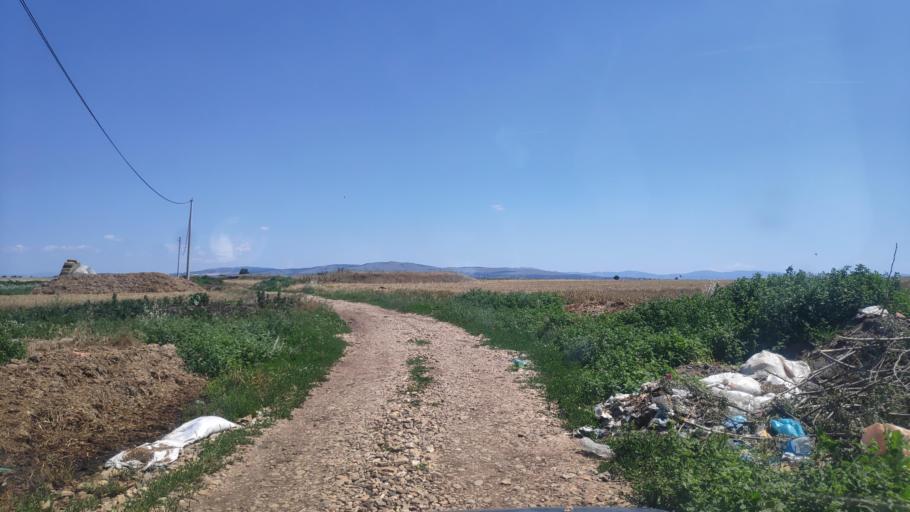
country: MK
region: Kumanovo
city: Bedinje
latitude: 42.1580
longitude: 21.6814
